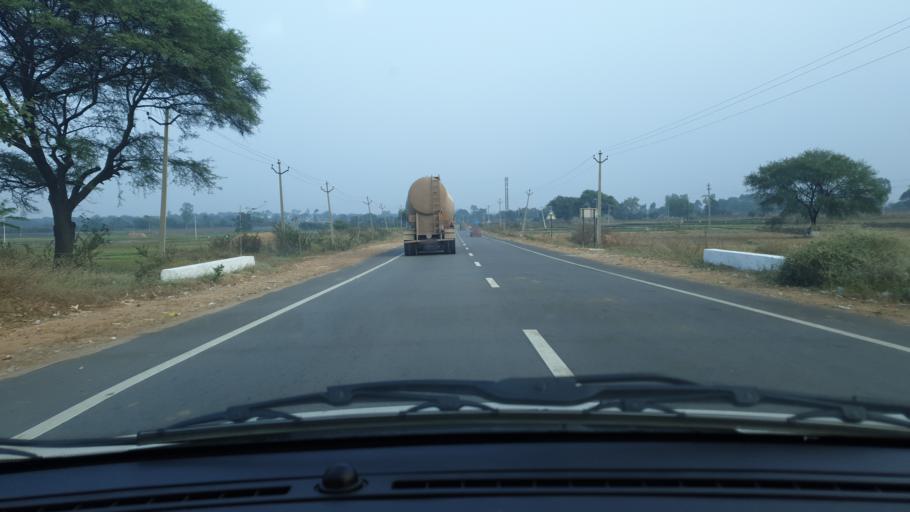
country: IN
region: Telangana
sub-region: Rangareddi
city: Vikarabad
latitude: 17.1640
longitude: 77.8300
